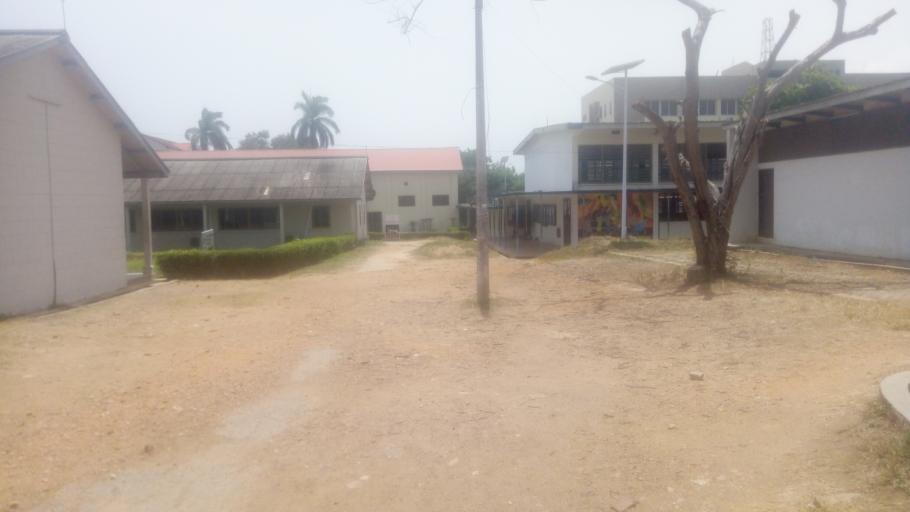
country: GH
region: Central
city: Winneba
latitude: 5.3621
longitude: -0.6323
